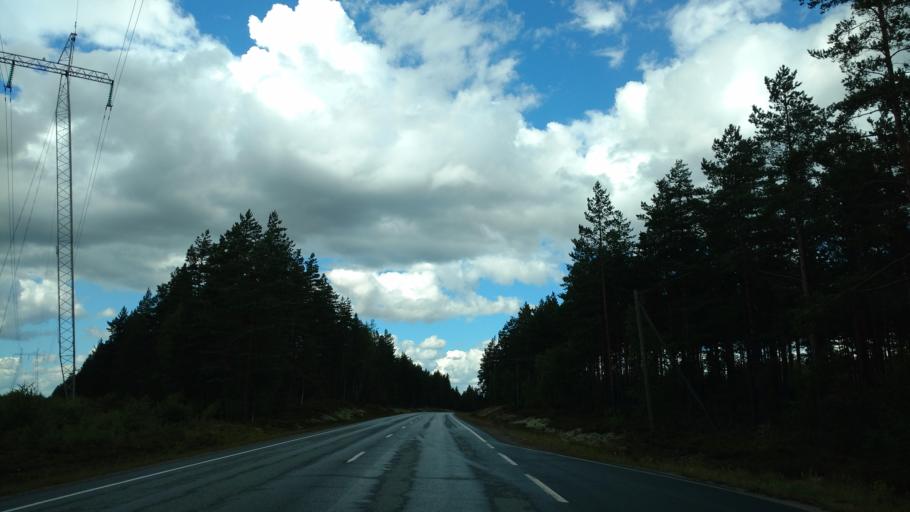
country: FI
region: Varsinais-Suomi
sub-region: Salo
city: Muurla
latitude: 60.2943
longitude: 23.3350
